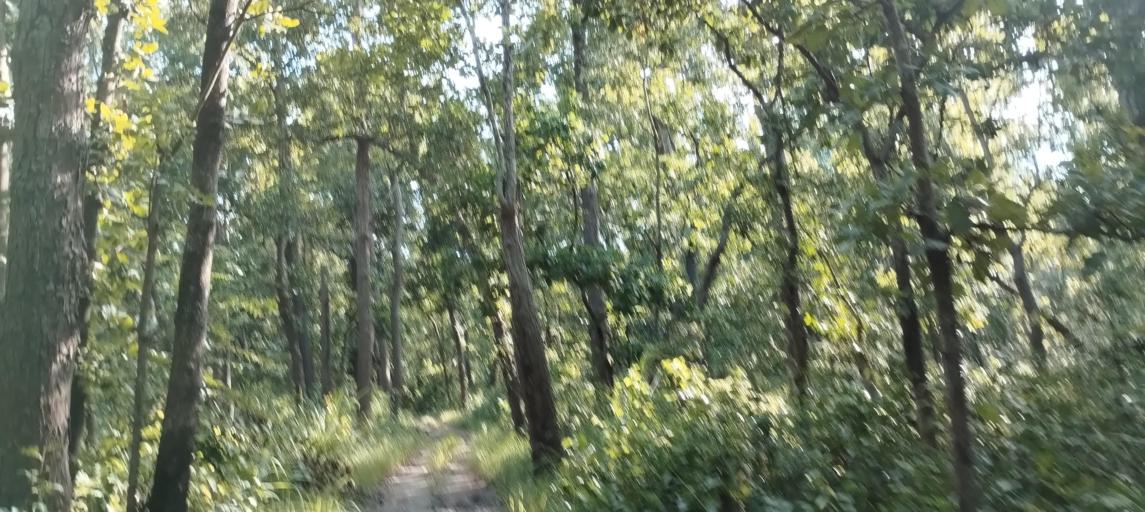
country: NP
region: Far Western
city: Tikapur
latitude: 28.5362
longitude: 81.2838
